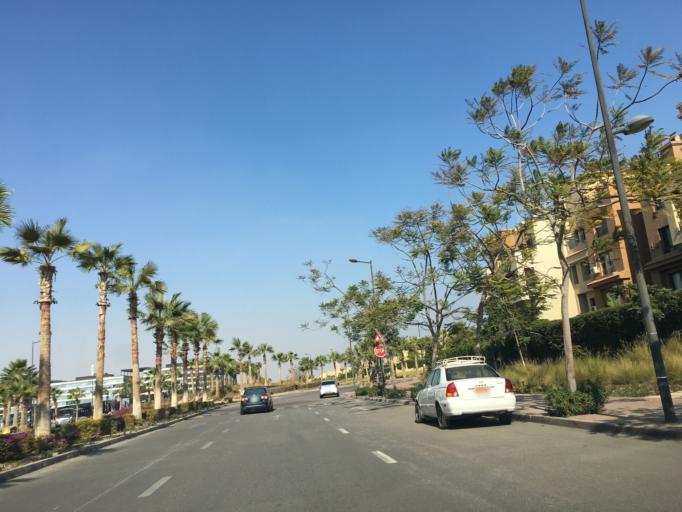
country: EG
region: Al Jizah
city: Awsim
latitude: 30.0669
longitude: 30.9469
